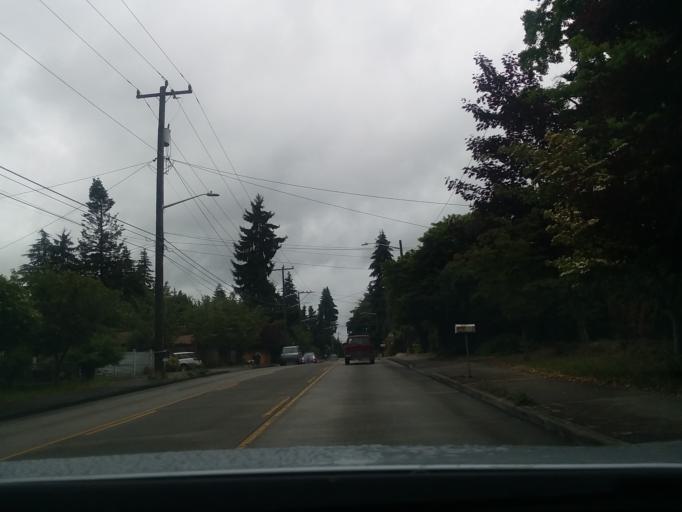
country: US
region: Washington
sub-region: King County
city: Lake Forest Park
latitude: 47.7085
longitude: -122.3067
